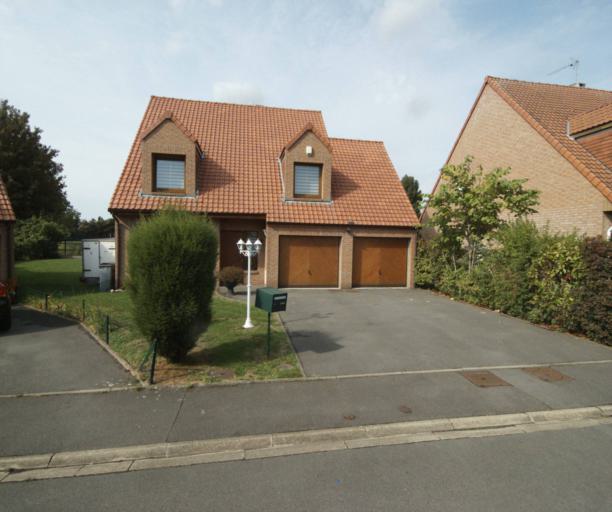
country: FR
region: Nord-Pas-de-Calais
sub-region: Departement du Nord
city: Marquette-lez-Lille
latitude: 50.6797
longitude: 3.0696
